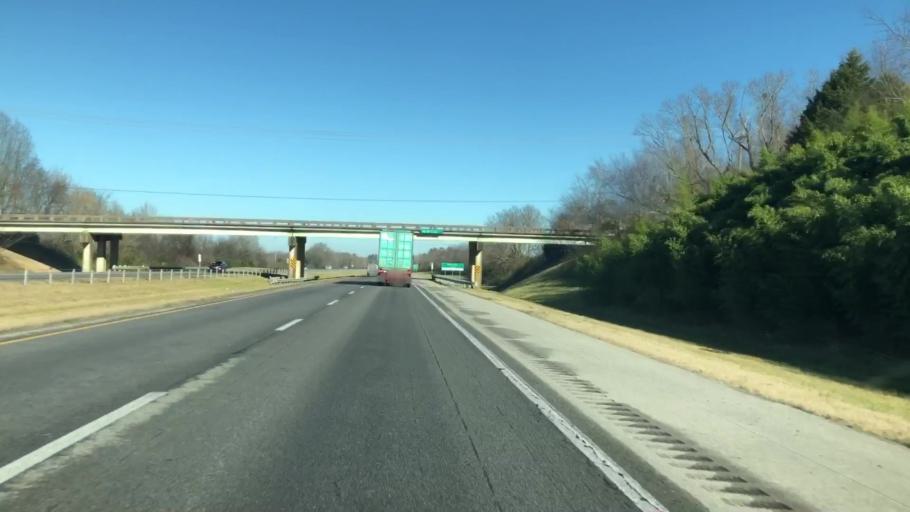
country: US
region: Alabama
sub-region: Limestone County
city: Athens
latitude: 34.8104
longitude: -86.9386
